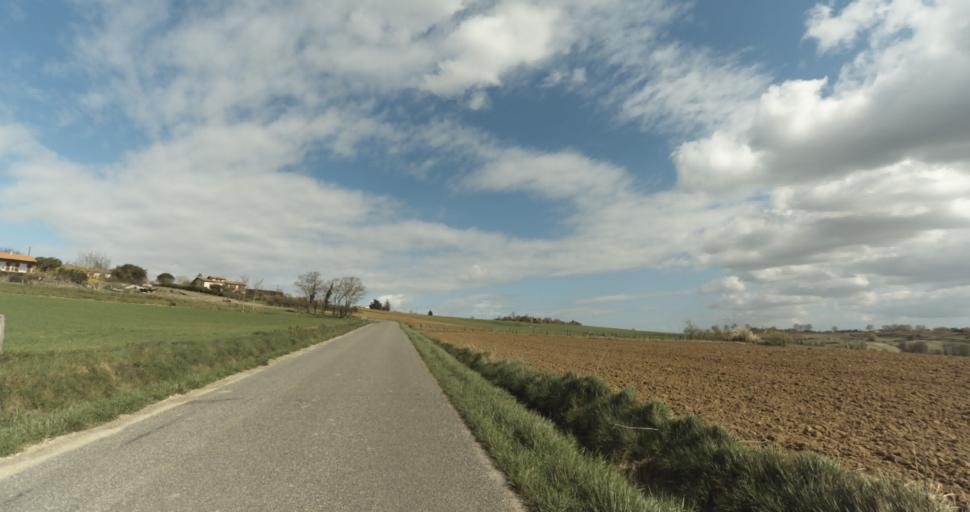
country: FR
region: Midi-Pyrenees
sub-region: Departement de la Haute-Garonne
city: Auterive
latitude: 43.3649
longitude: 1.4835
